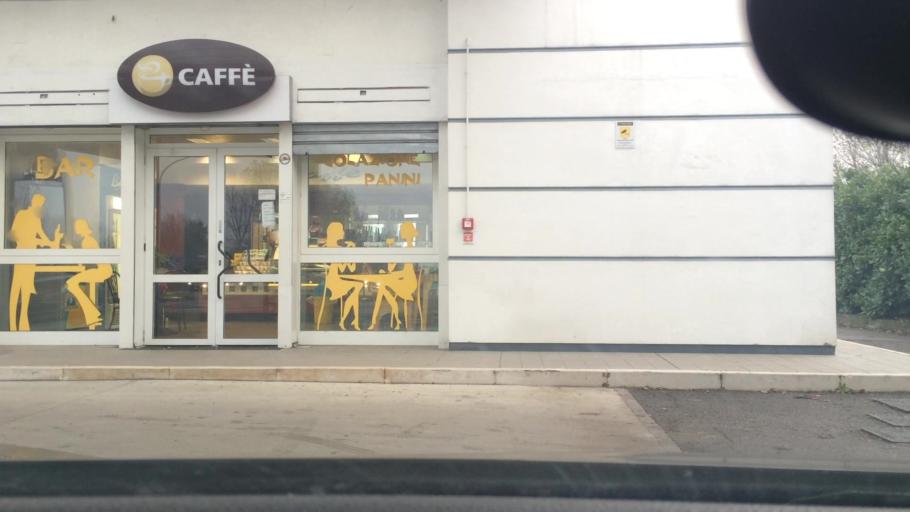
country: IT
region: Lombardy
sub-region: Citta metropolitana di Milano
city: Pogliano Milanese
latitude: 45.5364
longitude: 8.9972
